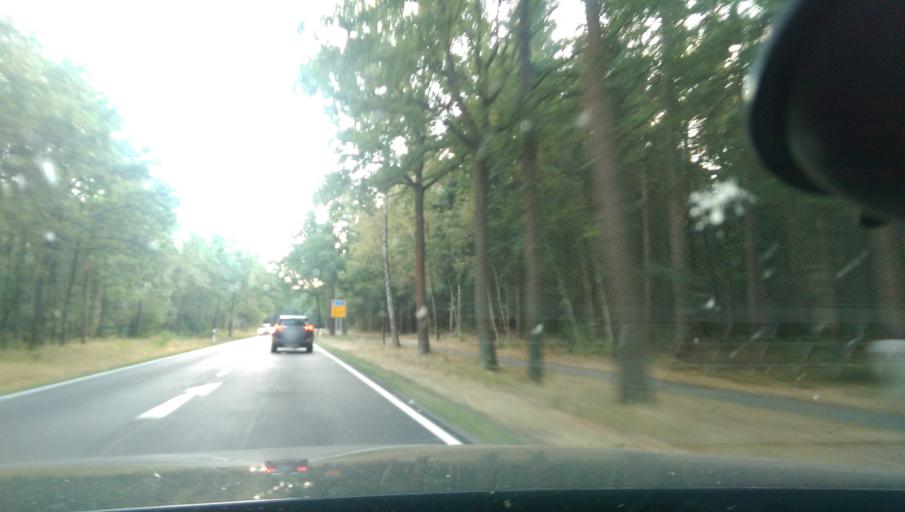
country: DE
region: Lower Saxony
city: Hodenhagen
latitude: 52.7787
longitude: 9.5800
